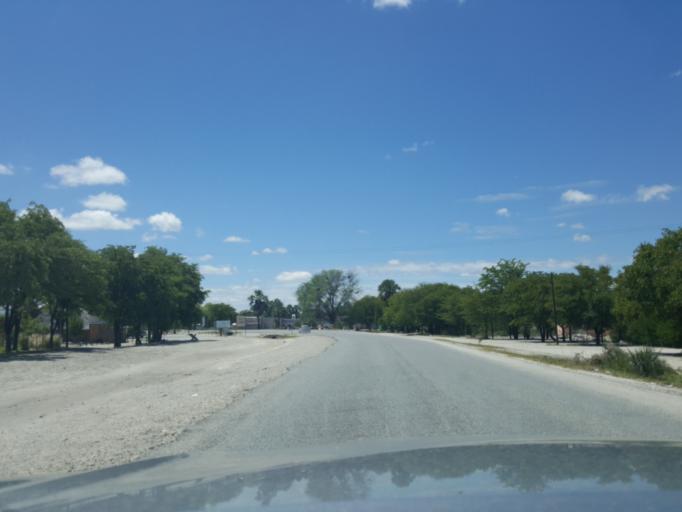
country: BW
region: Central
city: Nata
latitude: -20.2120
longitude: 26.1779
